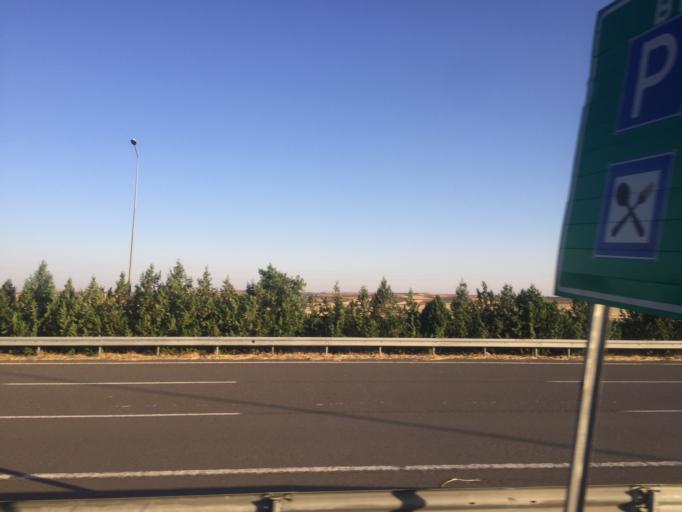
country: TR
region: Sanliurfa
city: Bogurtlen
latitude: 37.1001
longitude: 38.1958
